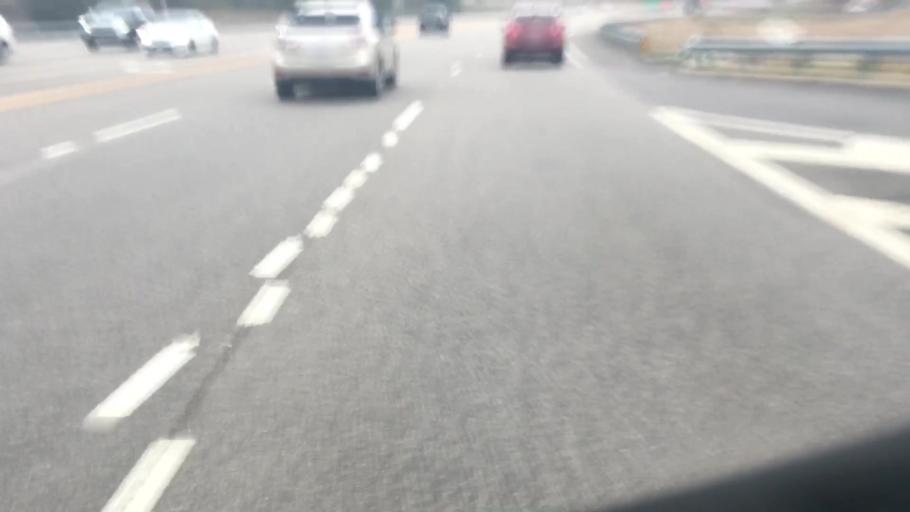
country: US
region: Alabama
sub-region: Shelby County
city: Helena
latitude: 33.3574
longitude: -86.8556
